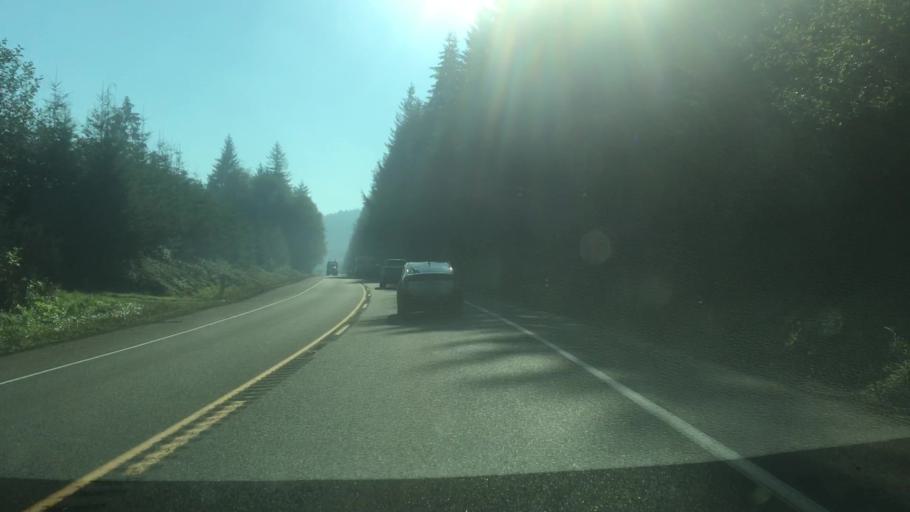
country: US
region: Washington
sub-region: Grays Harbor County
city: Central Park
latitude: 46.9267
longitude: -123.7162
